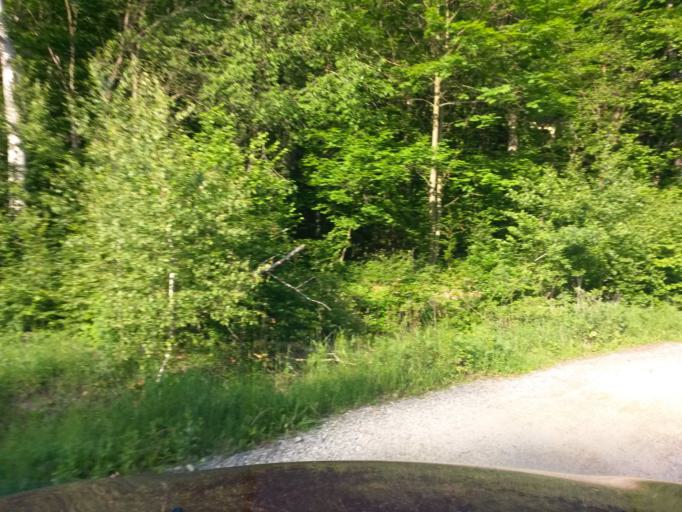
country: SK
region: Kosicky
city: Moldava nad Bodvou
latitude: 48.7460
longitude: 21.0269
